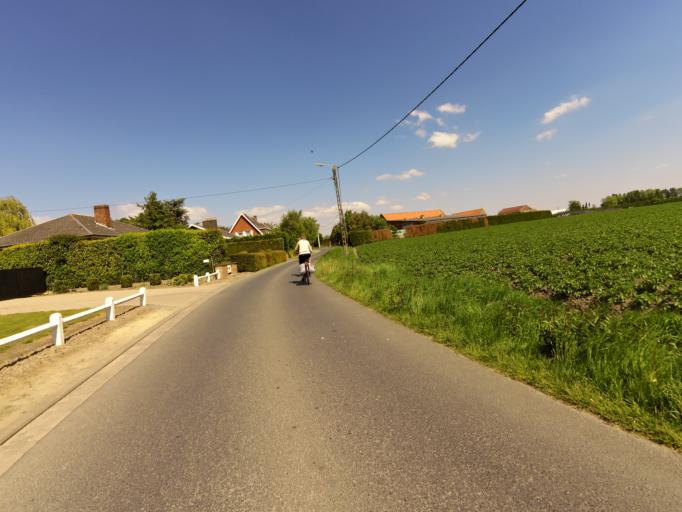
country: BE
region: Flanders
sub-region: Provincie West-Vlaanderen
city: Diksmuide
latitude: 51.0447
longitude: 2.9187
